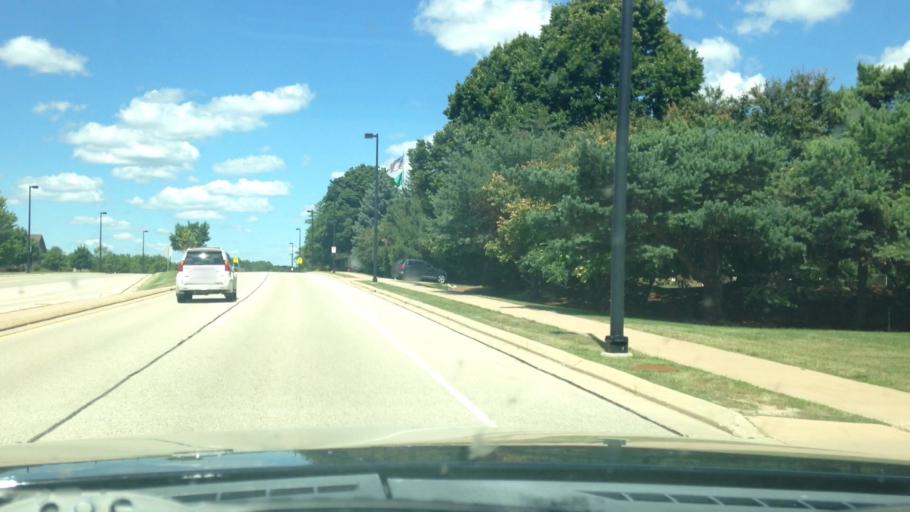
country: US
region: Wisconsin
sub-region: Waukesha County
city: Butler
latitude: 43.1494
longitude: -88.0753
